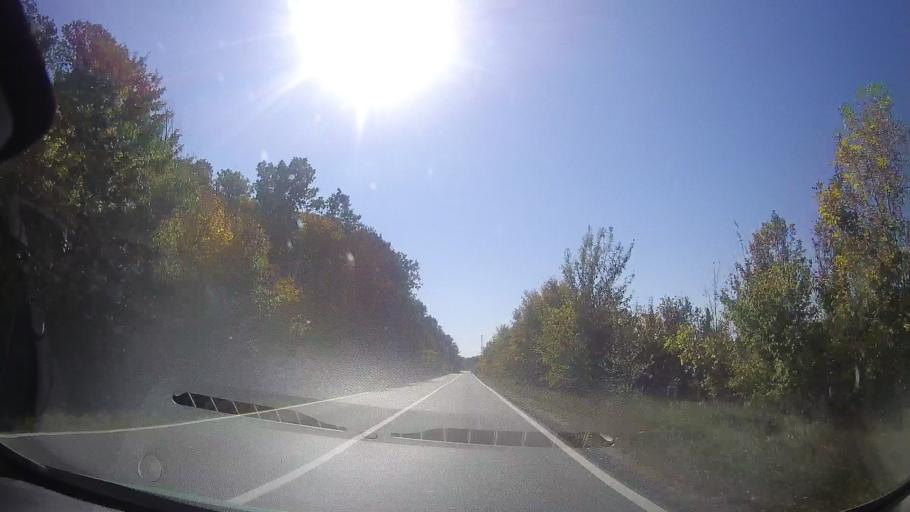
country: RO
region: Timis
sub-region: Municipiul Lugoj
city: Lugoj
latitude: 45.7118
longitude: 21.9670
